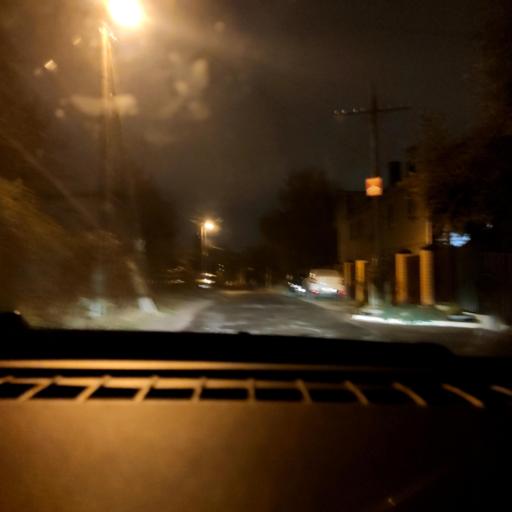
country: RU
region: Voronezj
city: Voronezh
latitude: 51.6681
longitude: 39.2593
